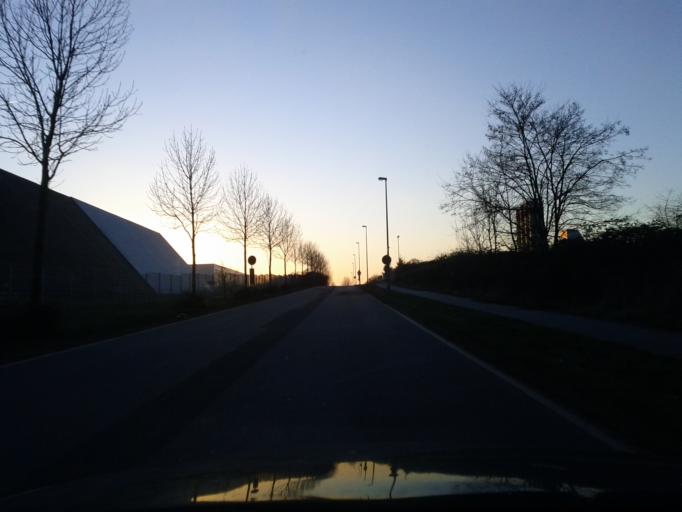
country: DE
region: Mecklenburg-Vorpommern
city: Wismar
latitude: 53.9057
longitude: 11.4618
